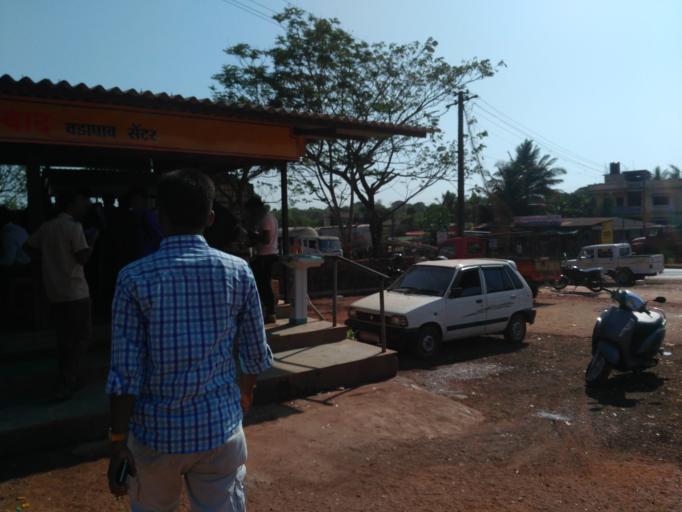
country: IN
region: Maharashtra
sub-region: Ratnagiri
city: Ratnagiri
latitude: 17.0413
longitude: 73.4220
